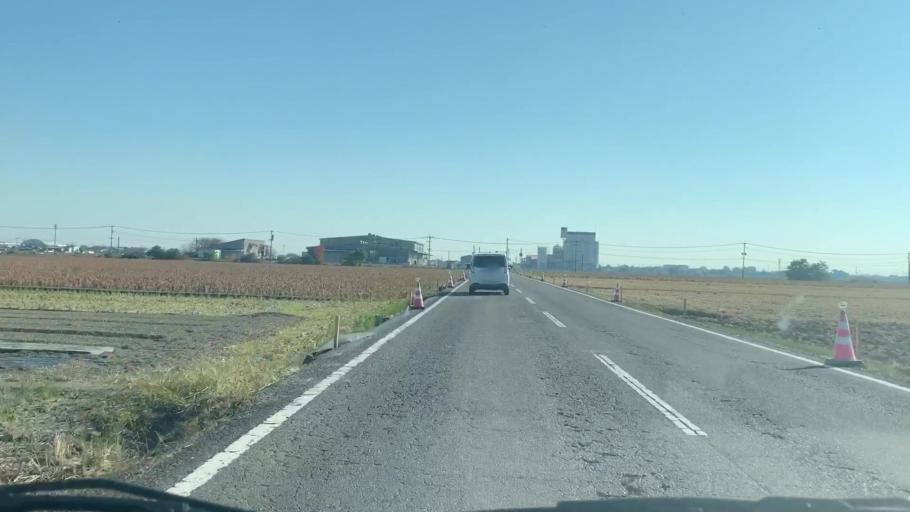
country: JP
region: Saga Prefecture
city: Saga-shi
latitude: 33.2277
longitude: 130.2815
